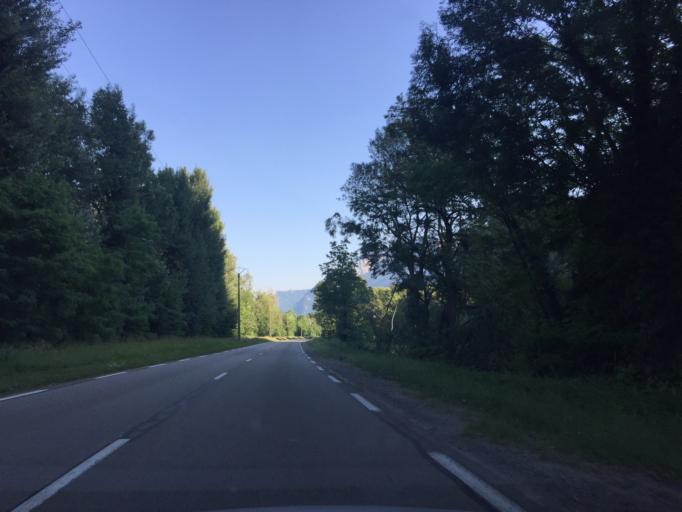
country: FR
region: Rhone-Alpes
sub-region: Departement de l'Isere
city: Voreppe
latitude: 45.2929
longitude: 5.6148
